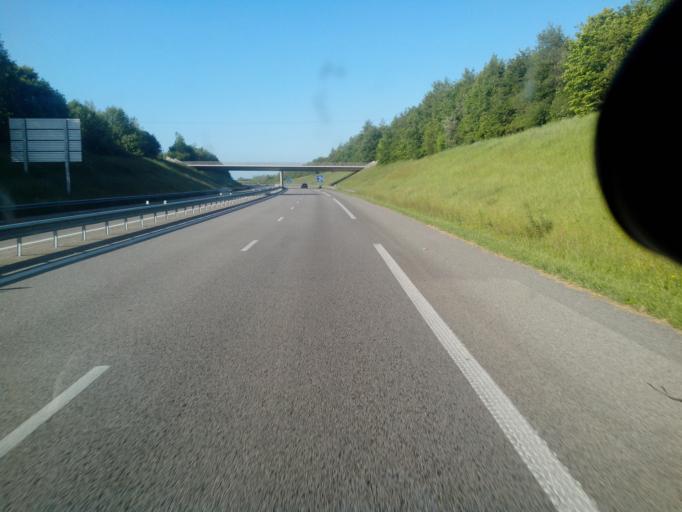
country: FR
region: Haute-Normandie
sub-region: Departement de la Seine-Maritime
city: Saint-Aubin-Routot
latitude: 49.5416
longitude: 0.3275
